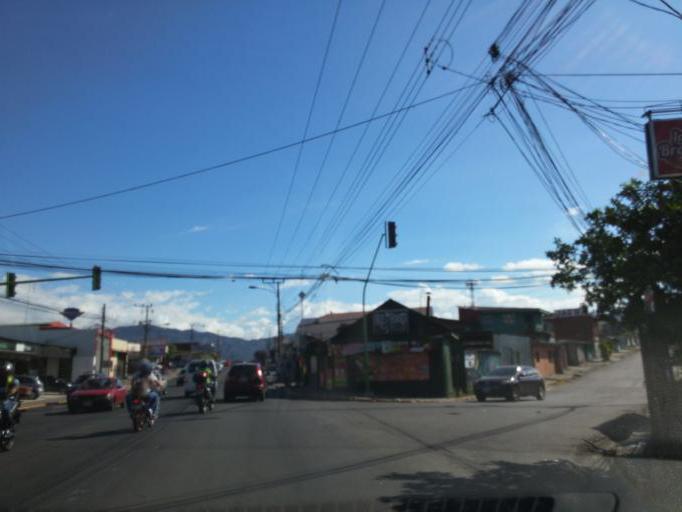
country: CR
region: San Jose
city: San Pedro
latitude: 9.9111
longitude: -84.0688
